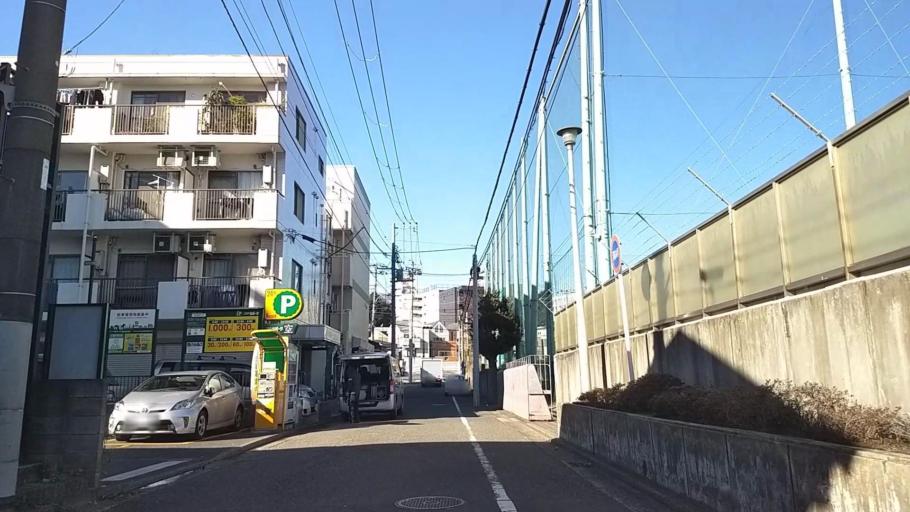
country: JP
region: Kanagawa
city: Yokohama
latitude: 35.4613
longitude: 139.6114
